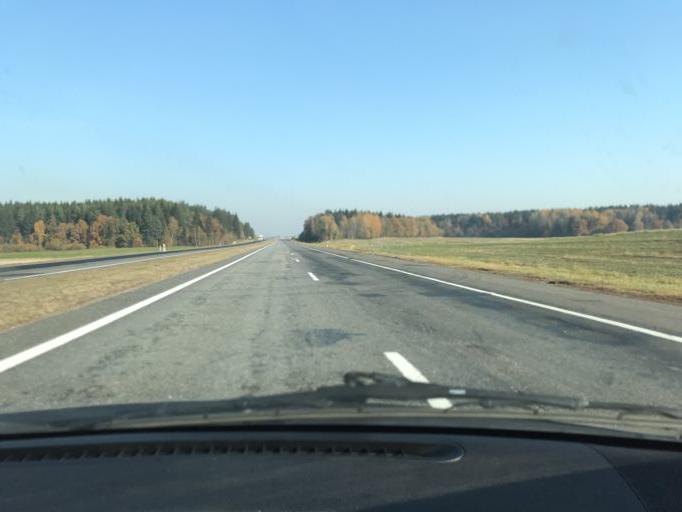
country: BY
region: Vitebsk
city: Horad Orsha
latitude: 54.5838
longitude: 30.3355
